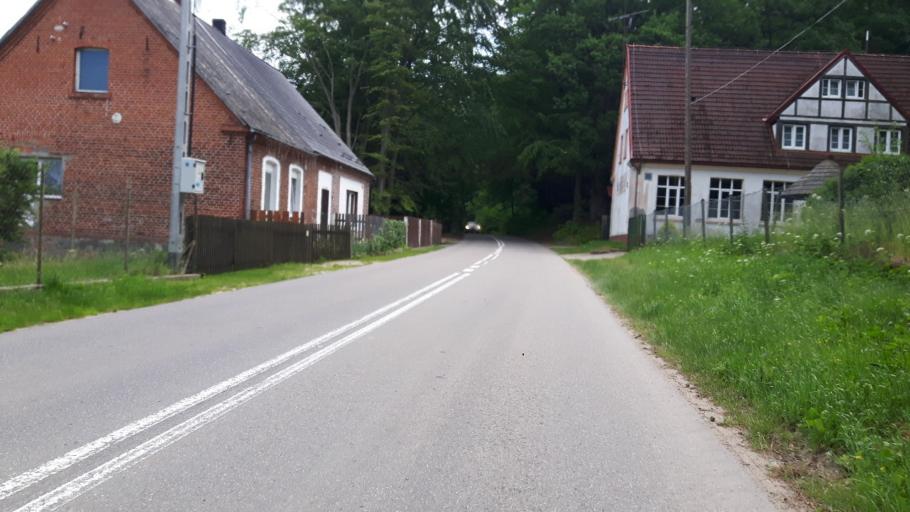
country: PL
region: Pomeranian Voivodeship
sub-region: Powiat leborski
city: Leba
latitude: 54.7552
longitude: 17.7022
